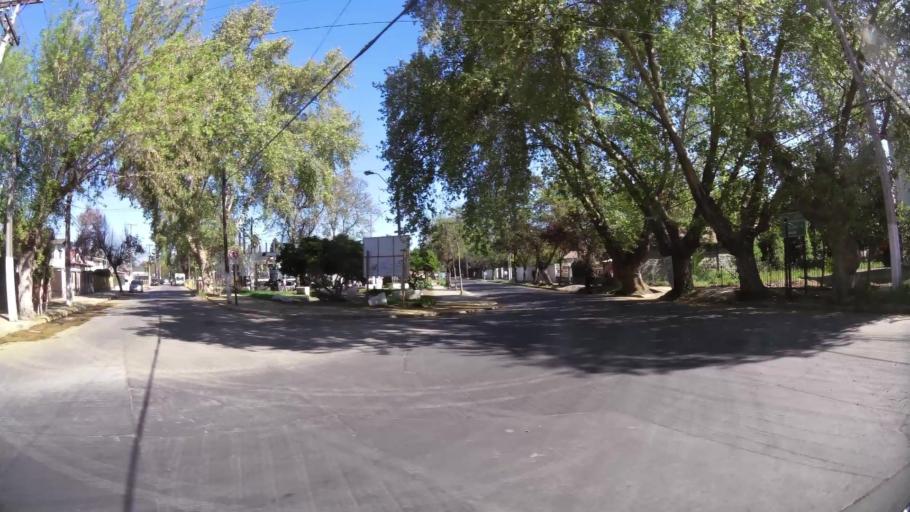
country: CL
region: Santiago Metropolitan
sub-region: Provincia de Talagante
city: Penaflor
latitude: -33.6052
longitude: -70.9019
